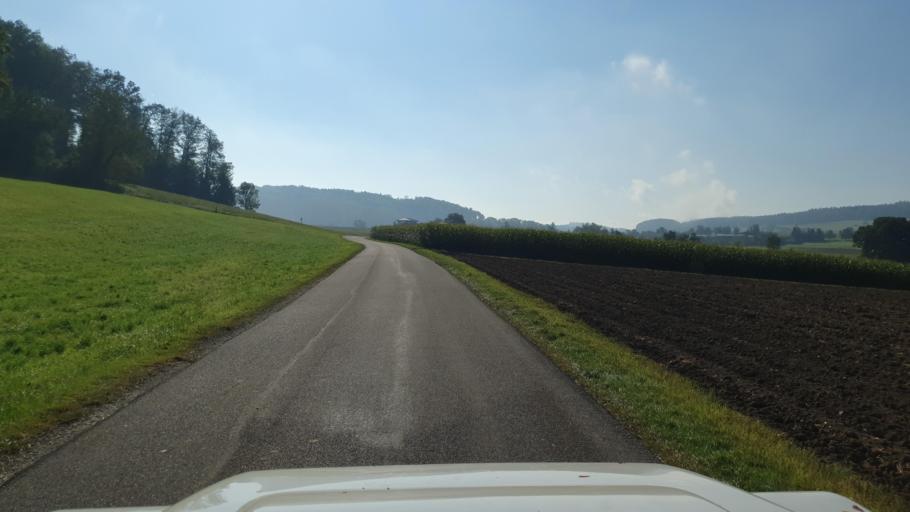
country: CH
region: Aargau
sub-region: Bezirk Bremgarten
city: Villmergen
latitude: 47.3328
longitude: 8.2600
